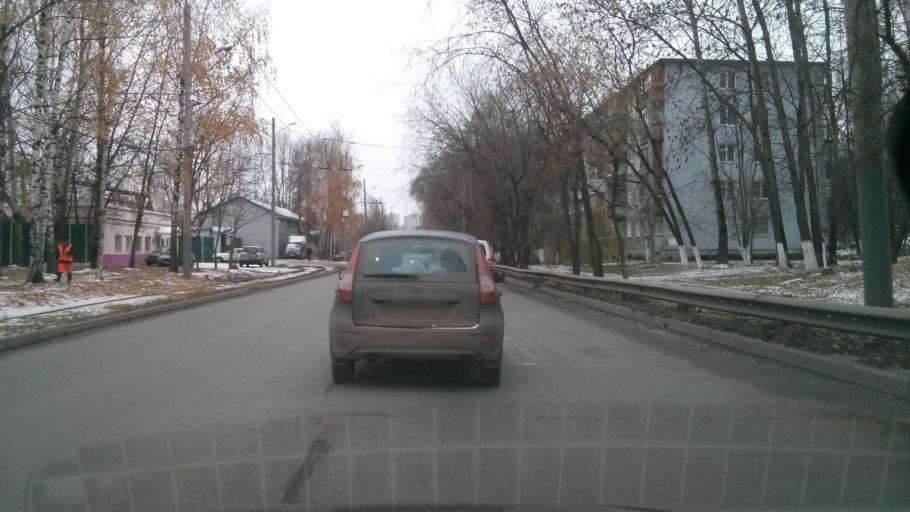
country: RU
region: Nizjnij Novgorod
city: Nizhniy Novgorod
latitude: 56.3003
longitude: 44.0484
